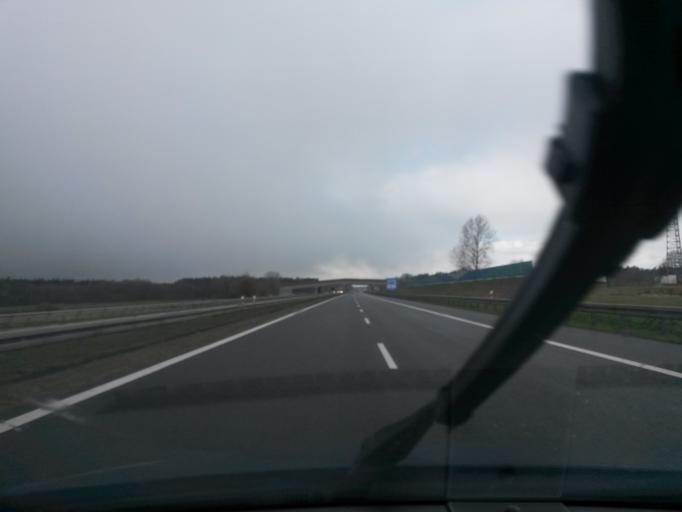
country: PL
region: Greater Poland Voivodeship
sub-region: Powiat koninski
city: Stare Miasto
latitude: 52.1714
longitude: 18.1592
